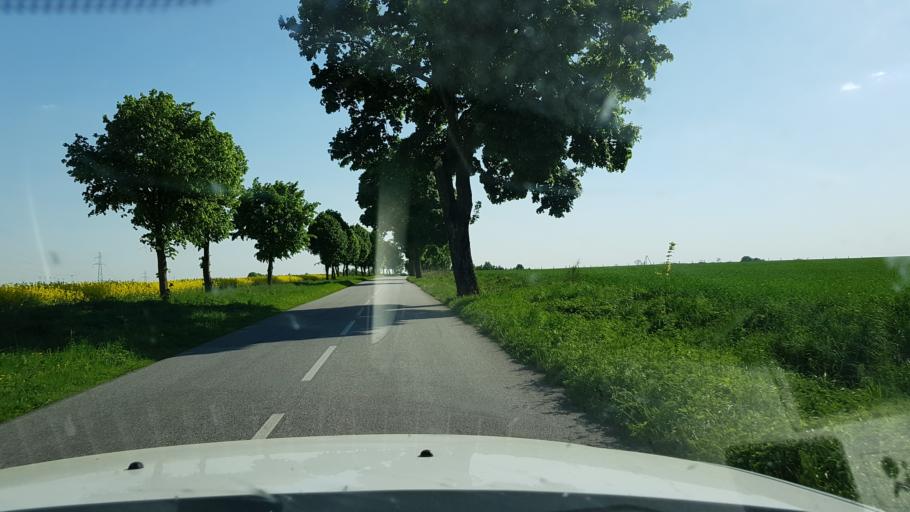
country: PL
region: West Pomeranian Voivodeship
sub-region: Powiat lobeski
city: Resko
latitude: 53.7957
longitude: 15.4141
